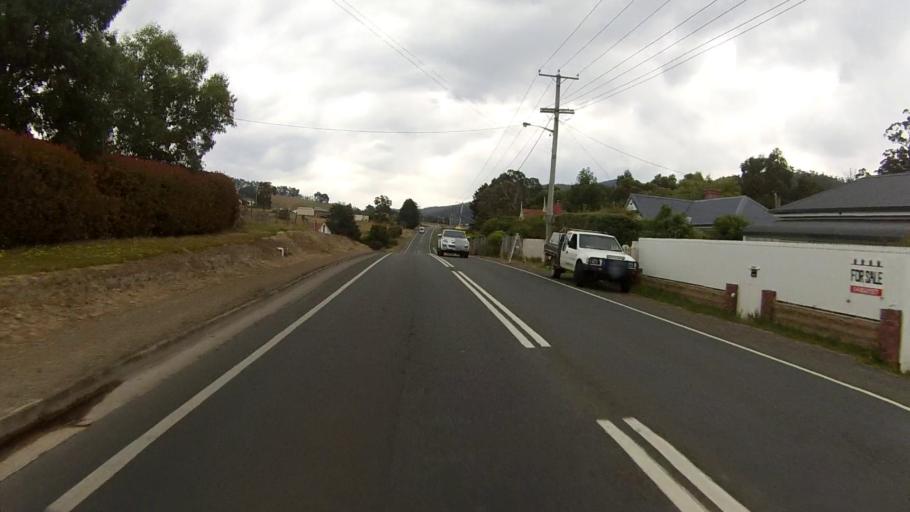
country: AU
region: Tasmania
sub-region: Huon Valley
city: Cygnet
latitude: -43.1518
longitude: 147.0708
